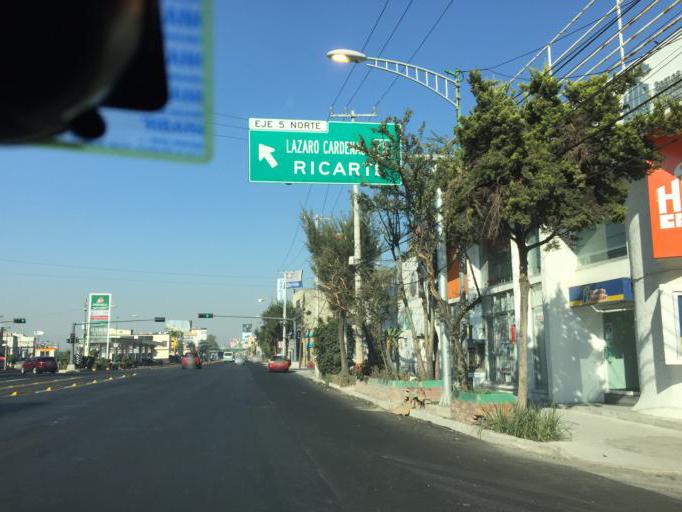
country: MX
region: Mexico
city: Colonia Lindavista
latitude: 19.4912
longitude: -99.1351
